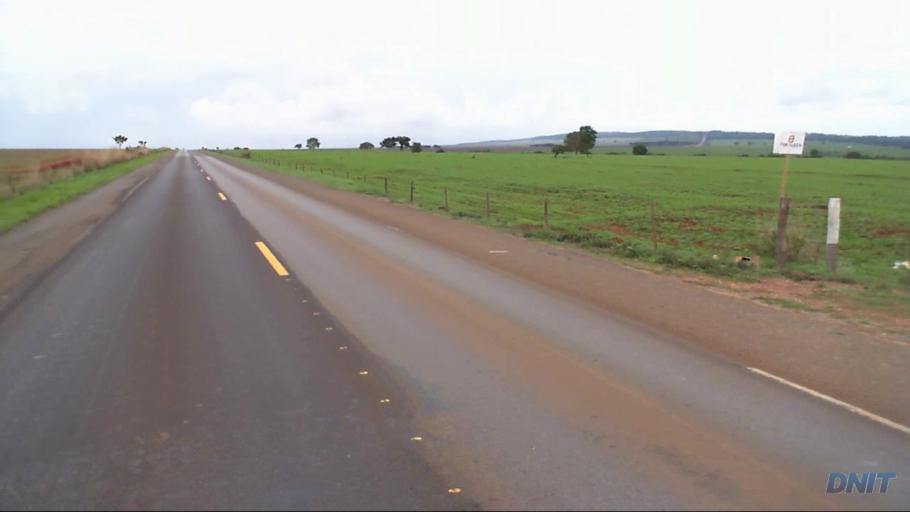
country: BR
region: Goias
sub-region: Padre Bernardo
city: Padre Bernardo
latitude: -15.1667
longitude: -48.3638
